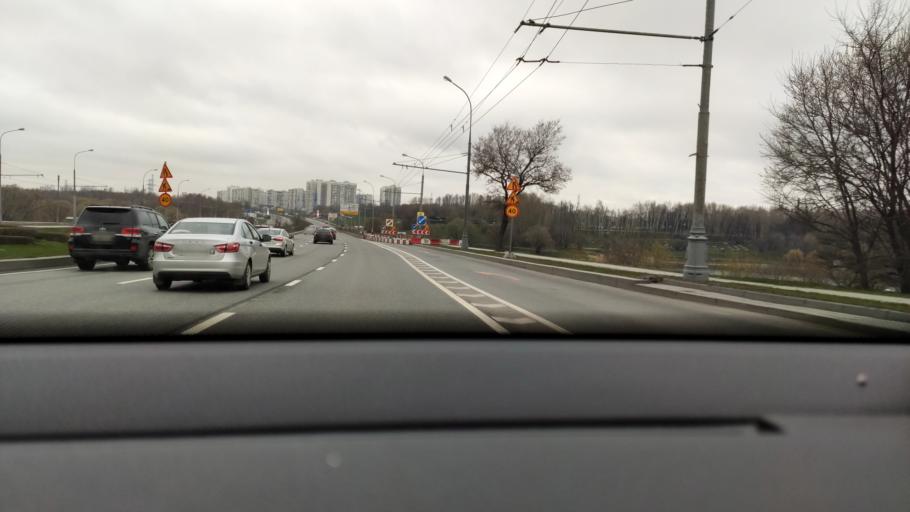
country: RU
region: Moscow
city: Mar'ino
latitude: 55.6281
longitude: 37.7092
